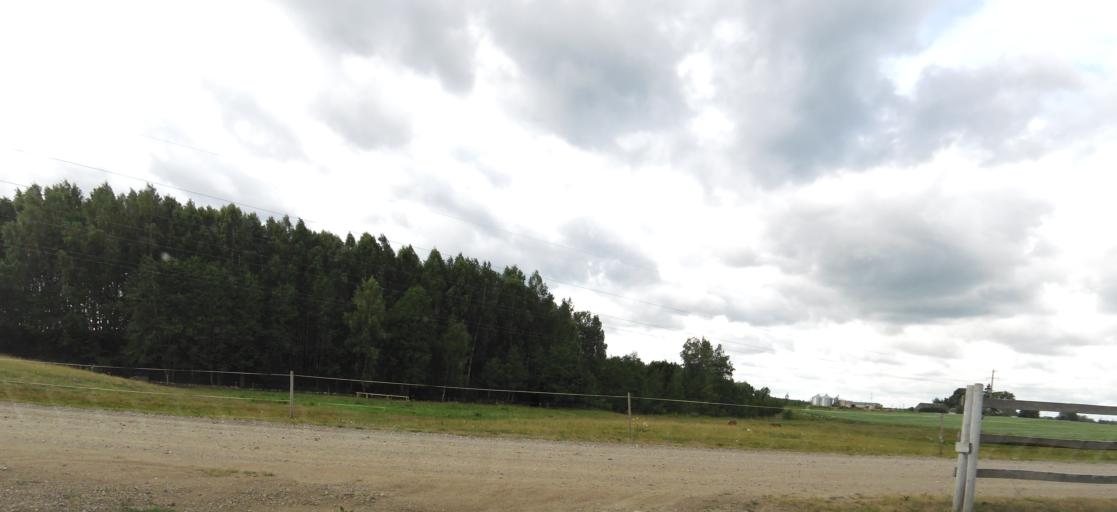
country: LT
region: Panevezys
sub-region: Birzai
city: Birzai
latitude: 56.2354
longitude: 24.7844
